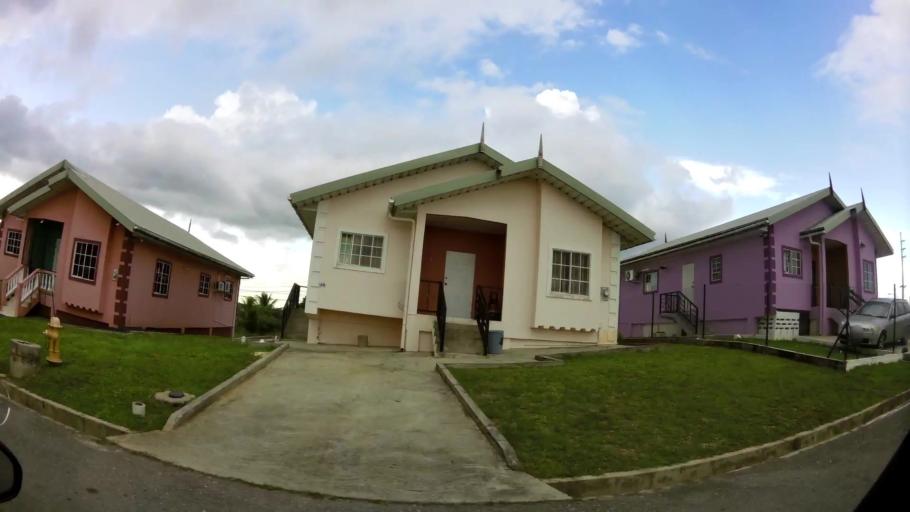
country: TT
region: City of San Fernando
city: Mon Repos
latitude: 10.2512
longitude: -61.4547
